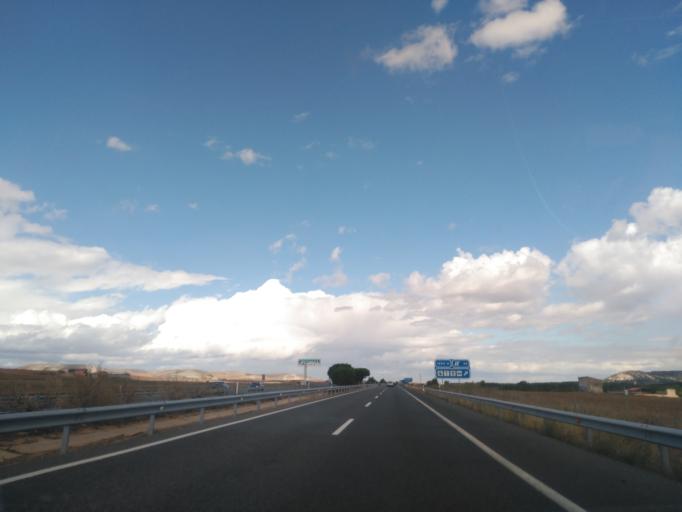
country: ES
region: Castille and Leon
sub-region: Provincia de Burgos
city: Villaquiran de los Infantes
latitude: 42.2260
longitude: -3.9968
